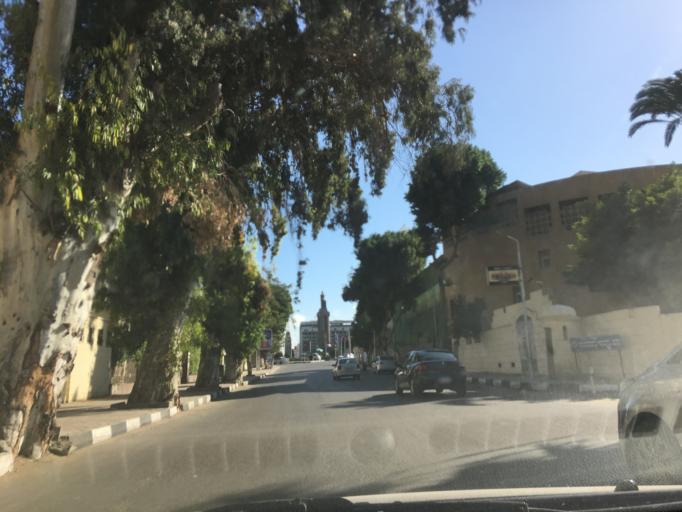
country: EG
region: Muhafazat al Qahirah
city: Cairo
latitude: 30.0439
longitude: 31.2254
